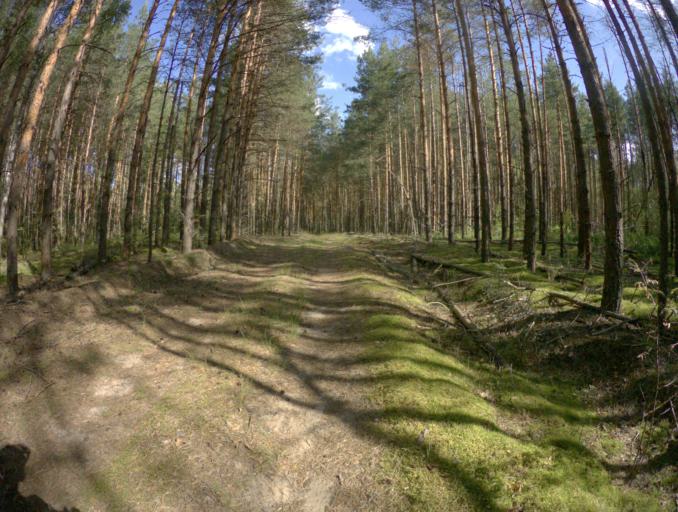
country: RU
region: Vladimir
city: Pokrov
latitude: 55.8471
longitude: 39.2191
